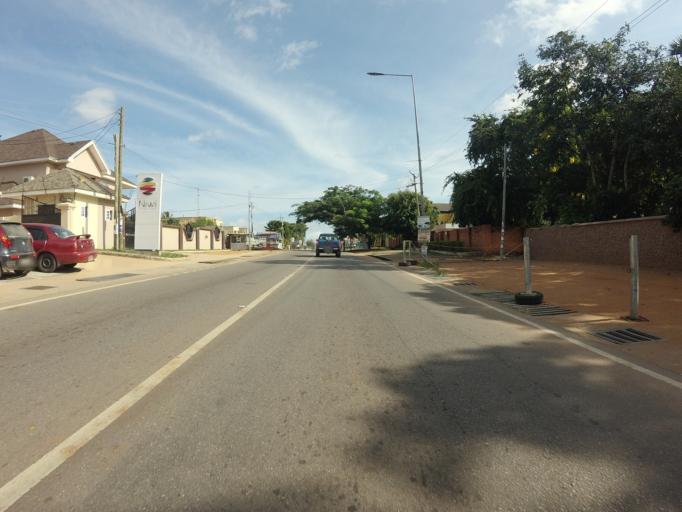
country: GH
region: Greater Accra
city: Medina Estates
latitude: 5.6394
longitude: -0.1619
